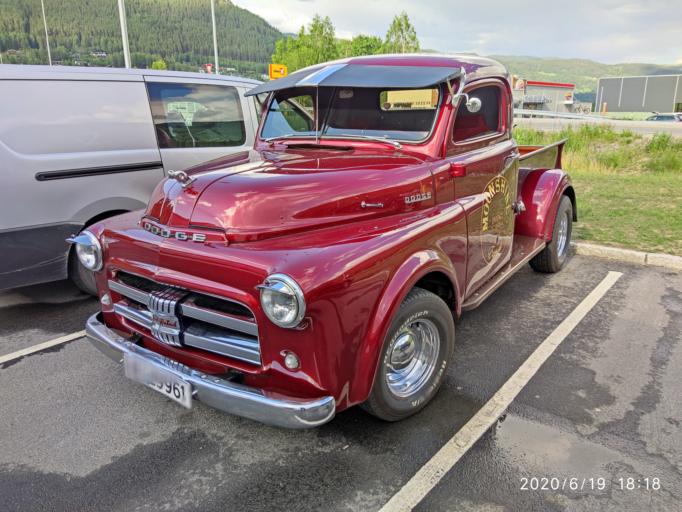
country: NO
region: Buskerud
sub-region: Gol
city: Gol
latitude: 60.6979
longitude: 8.9524
